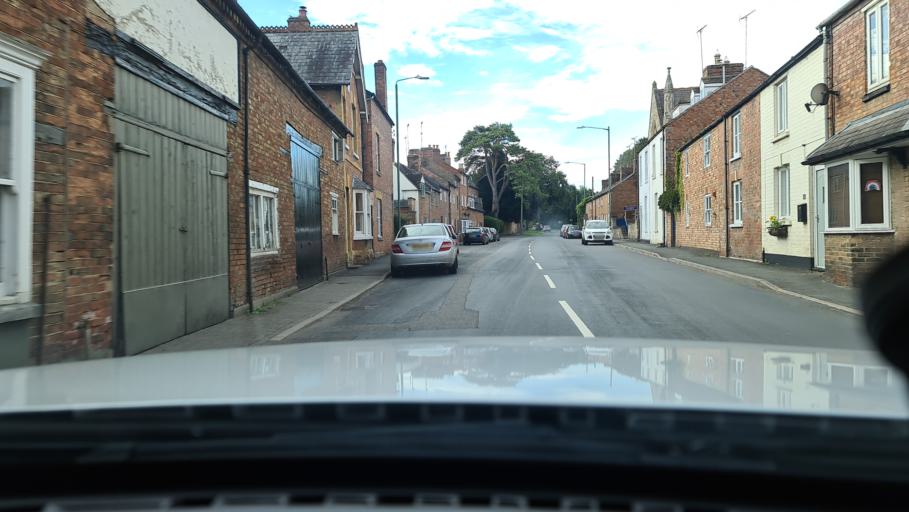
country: GB
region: England
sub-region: Warwickshire
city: Shipston on Stour
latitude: 52.0611
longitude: -1.6241
